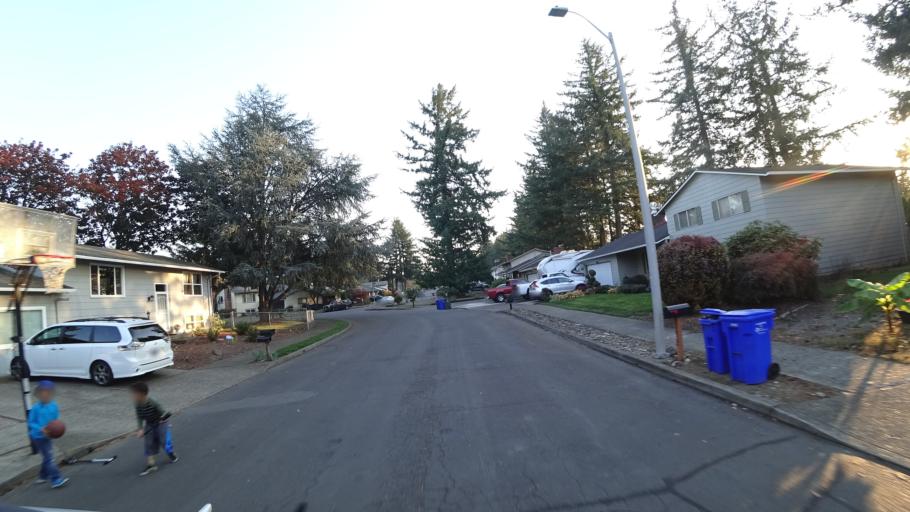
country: US
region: Oregon
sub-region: Multnomah County
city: Fairview
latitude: 45.5179
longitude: -122.4524
